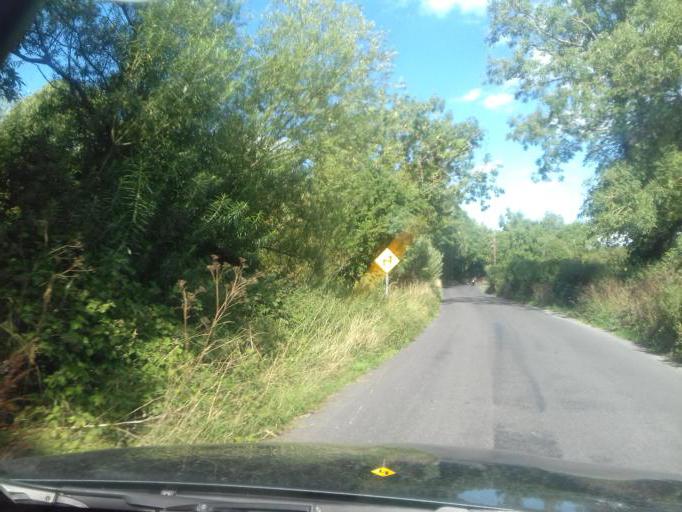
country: IE
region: Leinster
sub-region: Kilkenny
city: Kilkenny
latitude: 52.5393
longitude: -7.2587
